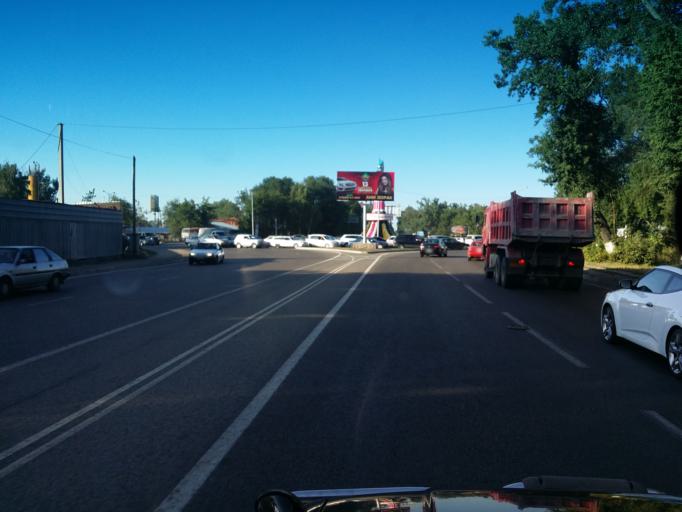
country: KZ
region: Almaty Oblysy
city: Pervomayskiy
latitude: 43.3190
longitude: 77.0250
